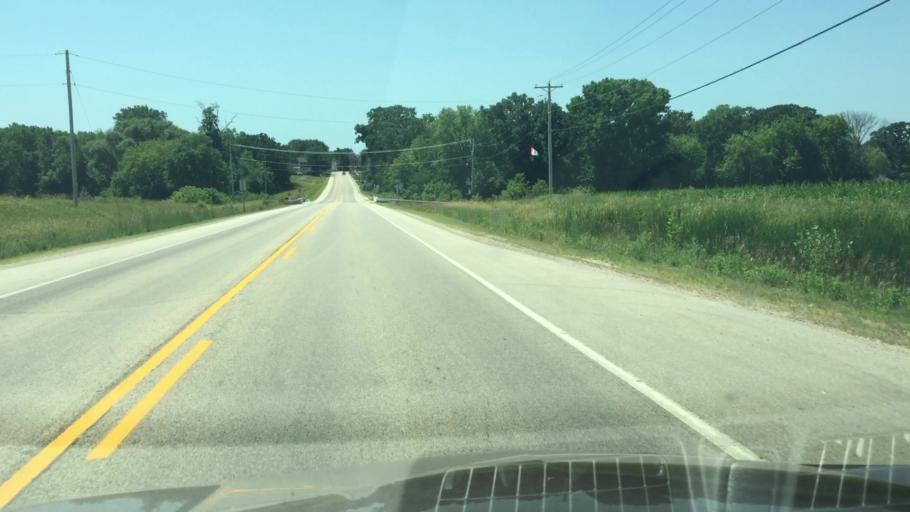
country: US
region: Wisconsin
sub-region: Fond du Lac County
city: Saint Peter
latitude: 43.9200
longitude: -88.3097
